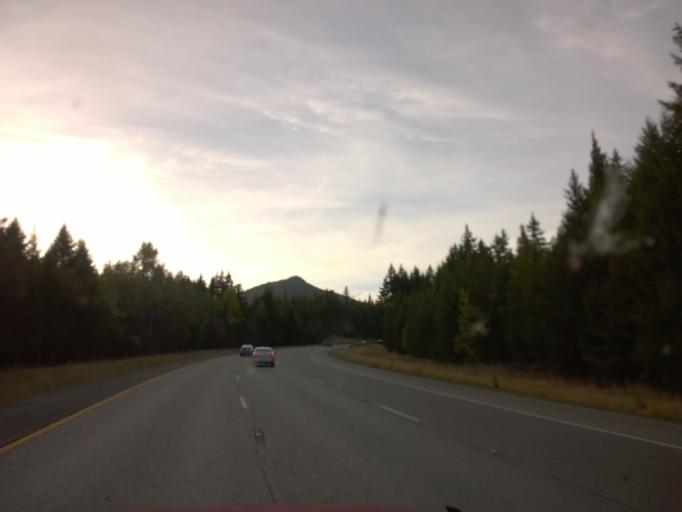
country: US
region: Washington
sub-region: Kittitas County
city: Cle Elum
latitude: 47.2581
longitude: -121.2085
